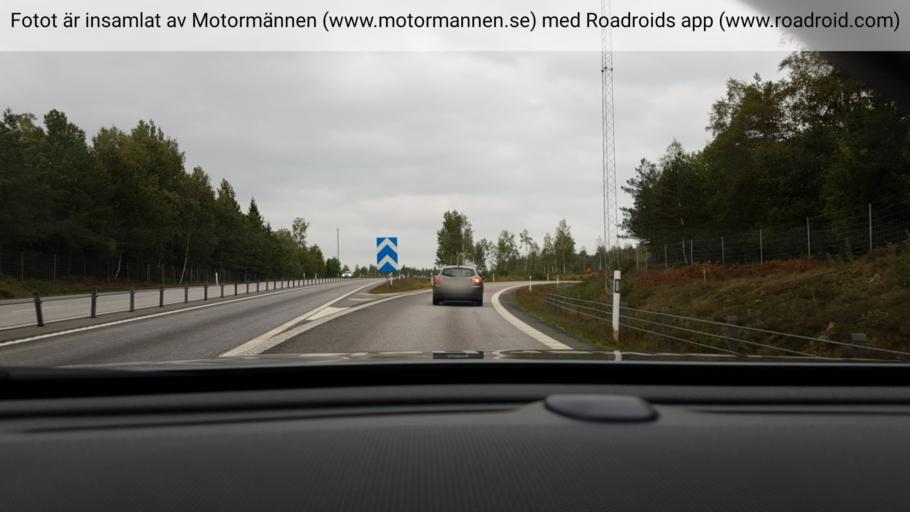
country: SE
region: Vaestra Goetaland
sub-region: Vanersborgs Kommun
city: Vanersborg
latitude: 58.3865
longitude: 12.2890
